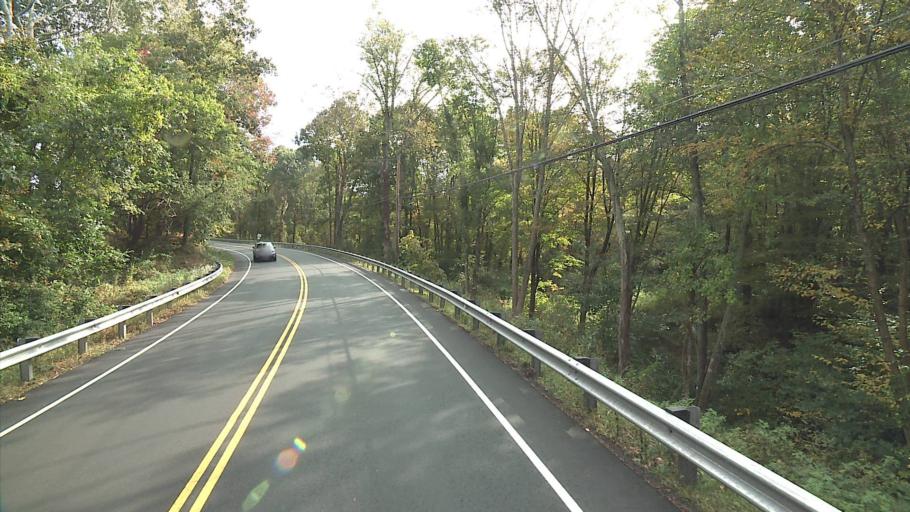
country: US
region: Connecticut
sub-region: Litchfield County
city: Watertown
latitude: 41.5982
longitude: -73.1516
